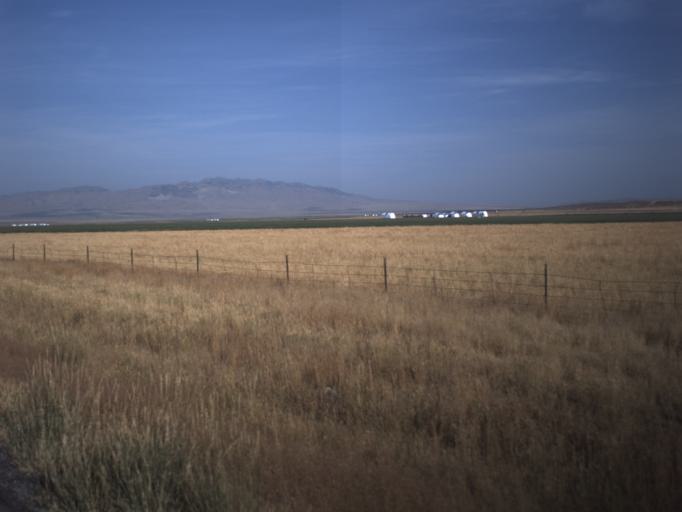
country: US
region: Idaho
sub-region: Oneida County
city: Malad City
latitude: 41.9670
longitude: -112.7942
